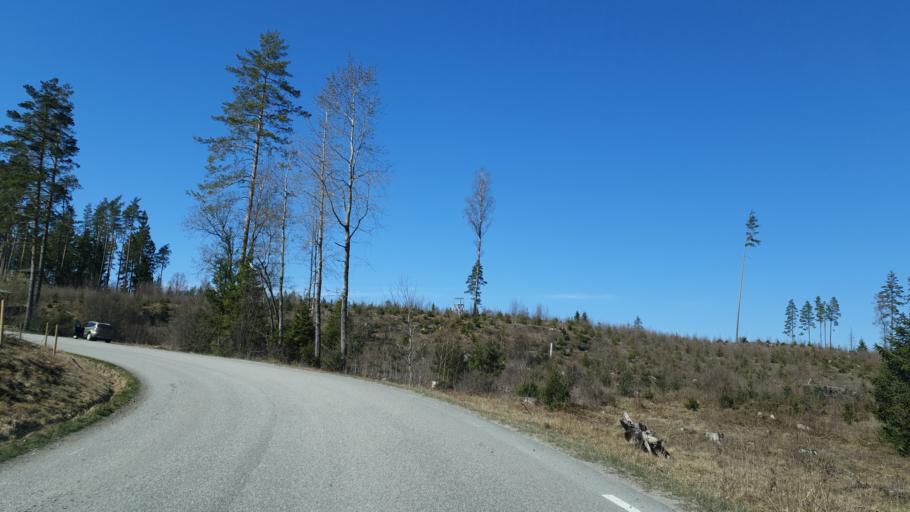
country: SE
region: Vaestra Goetaland
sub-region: Svenljunga Kommun
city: Svenljunga
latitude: 57.4399
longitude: 13.1385
